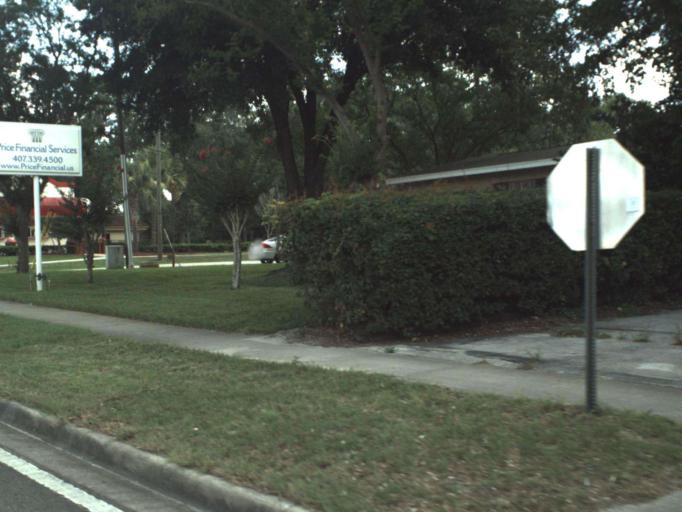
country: US
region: Florida
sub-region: Seminole County
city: Wekiwa Springs
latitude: 28.6788
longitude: -81.4189
